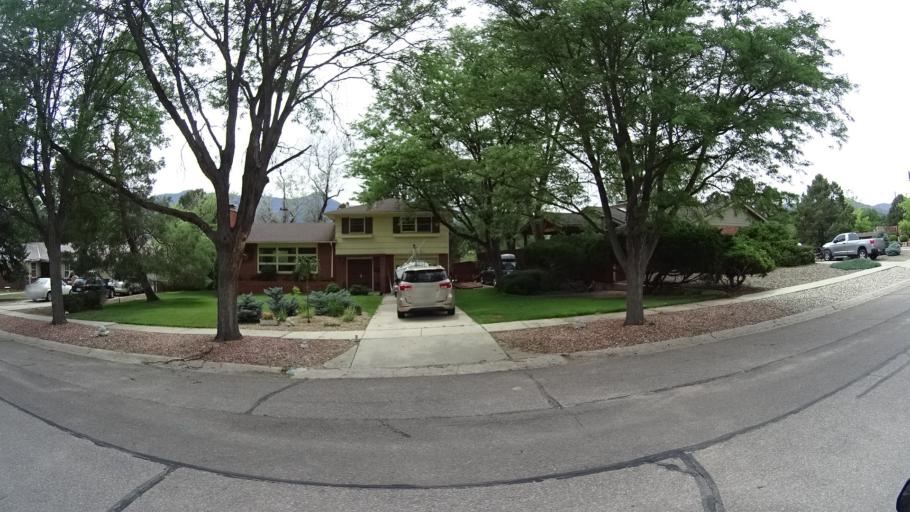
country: US
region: Colorado
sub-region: El Paso County
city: Colorado Springs
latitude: 38.8600
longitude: -104.8636
